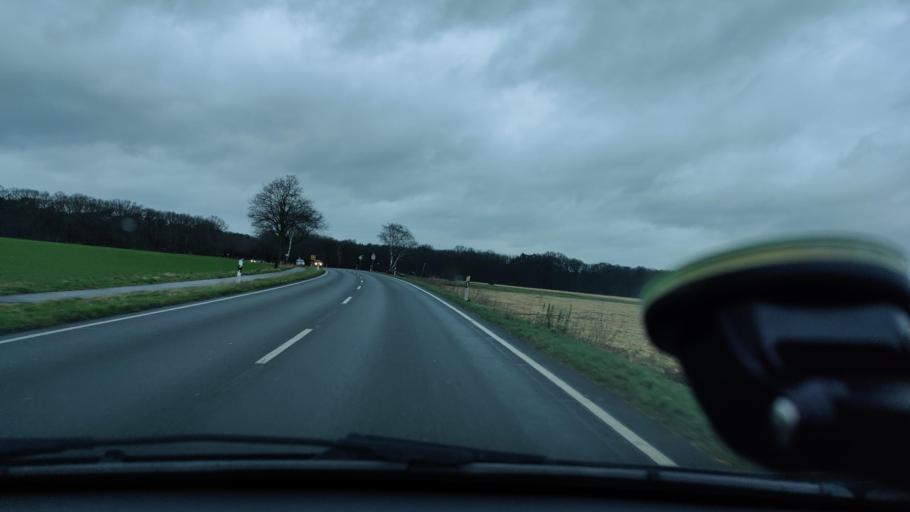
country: DE
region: North Rhine-Westphalia
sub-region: Regierungsbezirk Dusseldorf
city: Weeze
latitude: 51.5939
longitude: 6.1743
